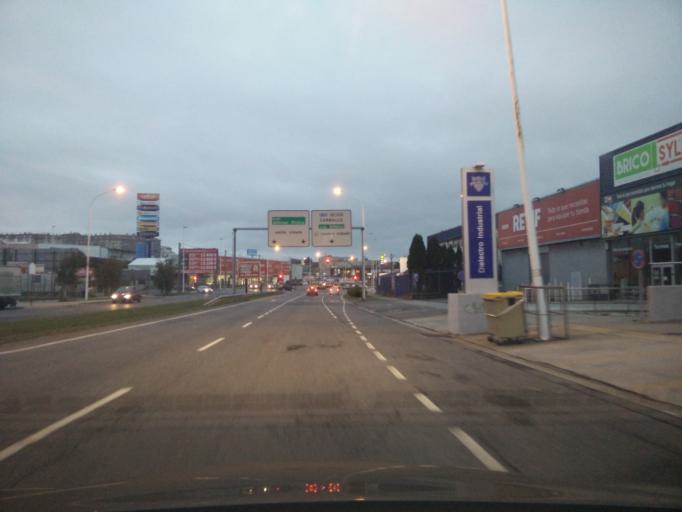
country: ES
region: Galicia
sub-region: Provincia da Coruna
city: A Coruna
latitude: 43.3507
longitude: -8.4246
